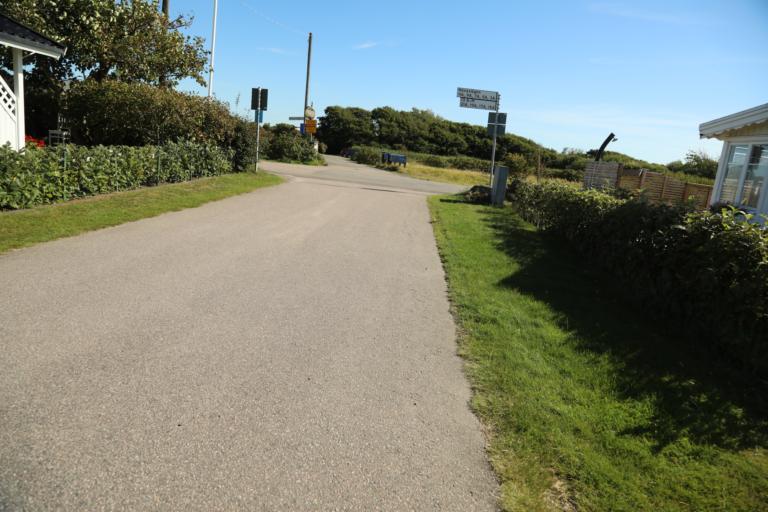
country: SE
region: Halland
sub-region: Varbergs Kommun
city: Traslovslage
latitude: 57.0823
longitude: 12.2650
